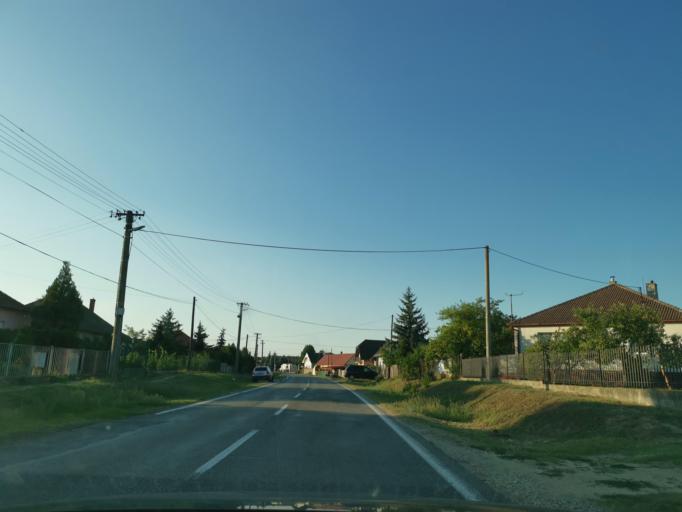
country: AT
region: Lower Austria
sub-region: Politischer Bezirk Mistelbach
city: Rabensburg
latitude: 48.6037
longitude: 16.9969
